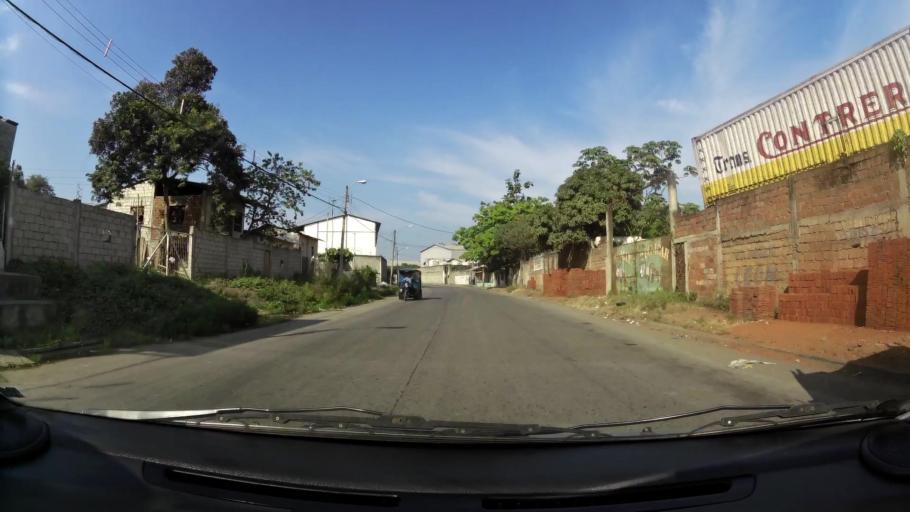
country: EC
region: Guayas
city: Santa Lucia
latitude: -2.0734
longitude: -79.9384
